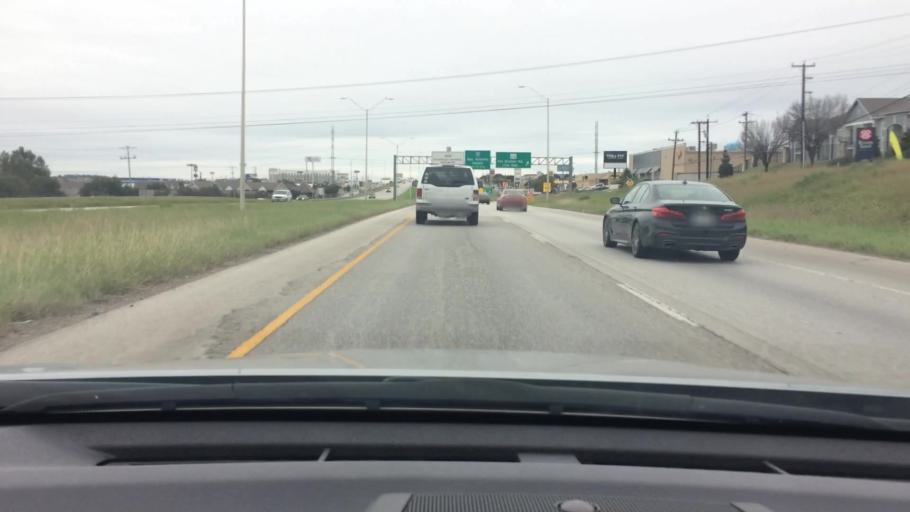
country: US
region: Texas
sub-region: Bexar County
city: Live Oak
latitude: 29.5558
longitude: -98.3238
